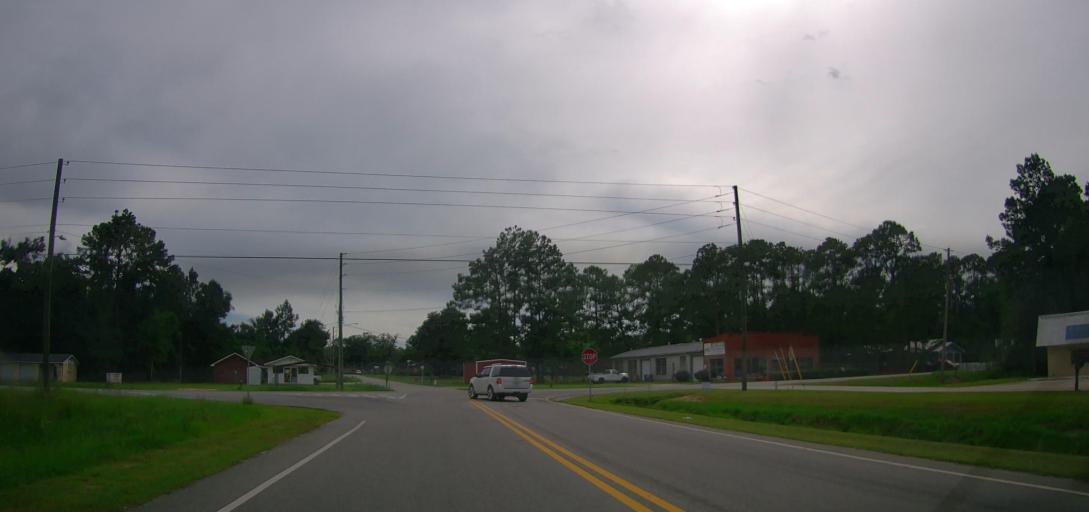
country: US
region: Georgia
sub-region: Wayne County
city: Jesup
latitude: 31.6155
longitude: -81.8945
